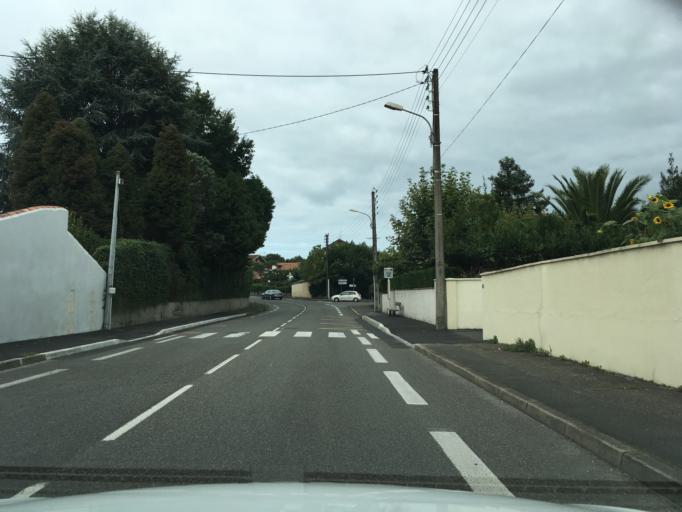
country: FR
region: Aquitaine
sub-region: Departement des Pyrenees-Atlantiques
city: Anglet
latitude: 43.4989
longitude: -1.5060
